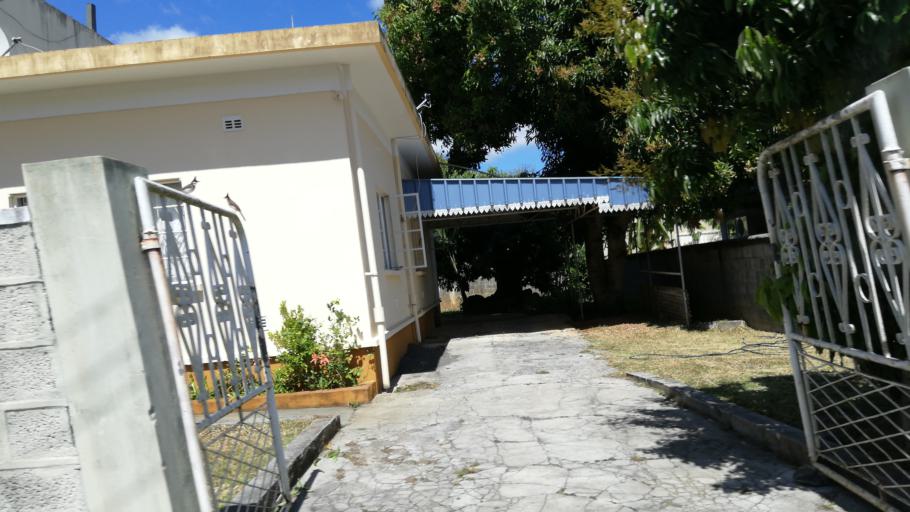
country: MU
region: Moka
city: Moka
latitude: -20.2280
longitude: 57.4726
